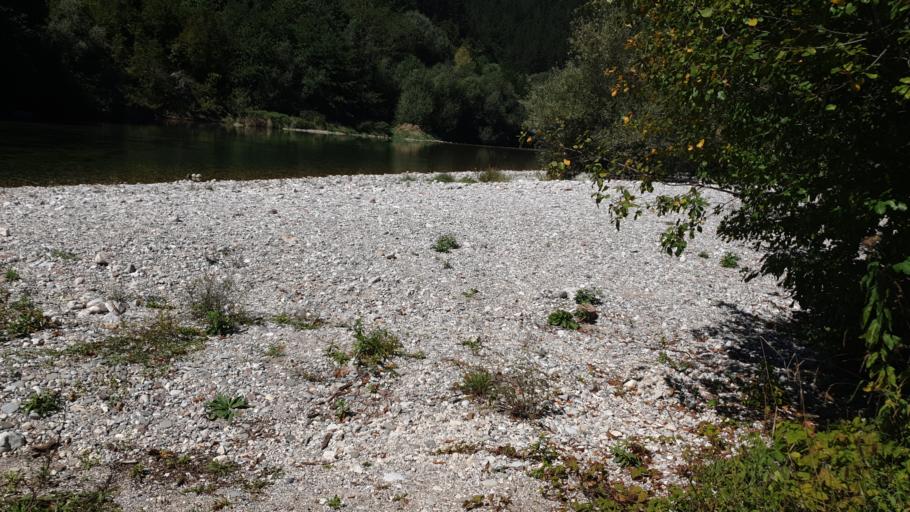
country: BA
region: Federation of Bosnia and Herzegovina
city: Polje-Bijela
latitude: 43.5239
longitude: 18.0823
